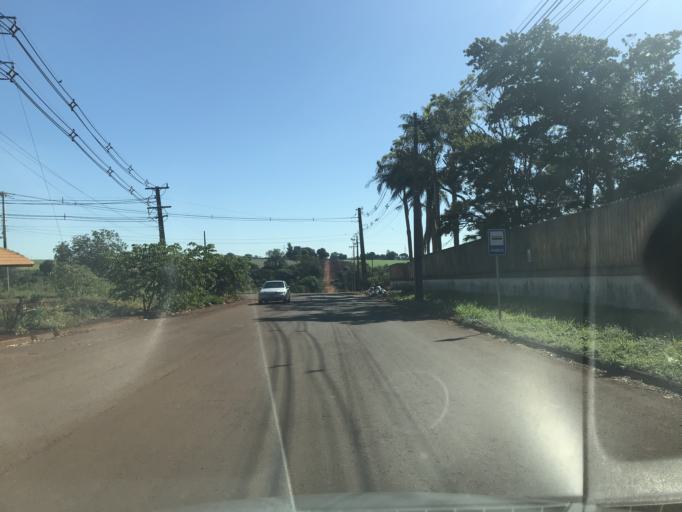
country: BR
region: Parana
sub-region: Palotina
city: Palotina
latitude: -24.2741
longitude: -53.8252
